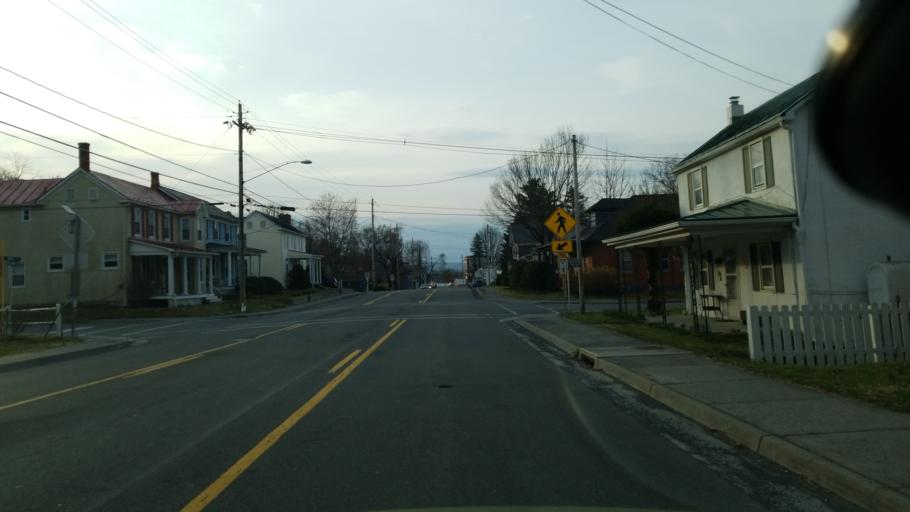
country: US
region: Virginia
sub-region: Clarke County
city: Berryville
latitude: 39.1547
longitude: -77.9865
